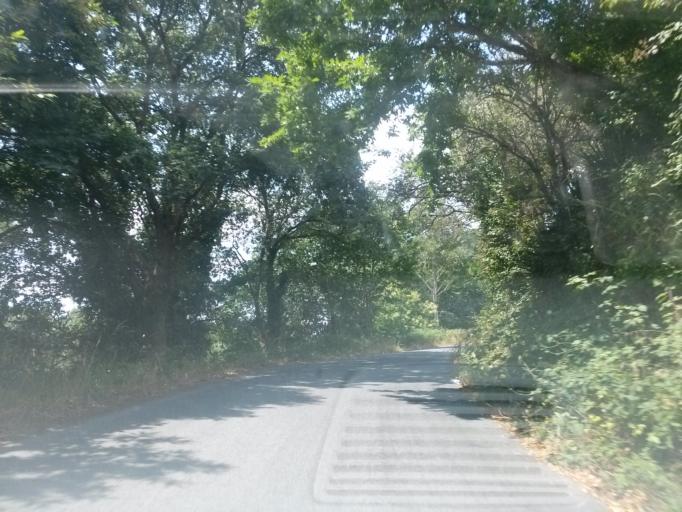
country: ES
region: Galicia
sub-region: Provincia de Lugo
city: Lugo
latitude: 43.0353
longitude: -7.5884
